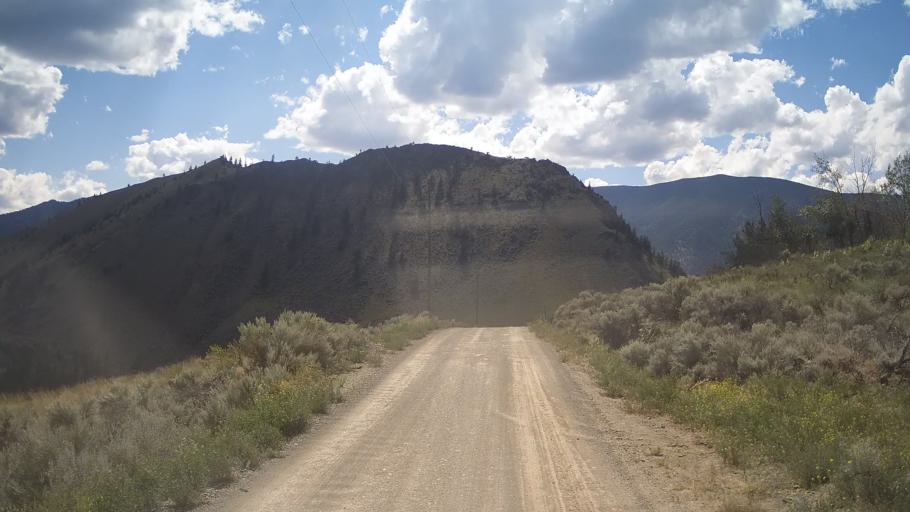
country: CA
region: British Columbia
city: Lillooet
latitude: 51.1988
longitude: -122.1025
